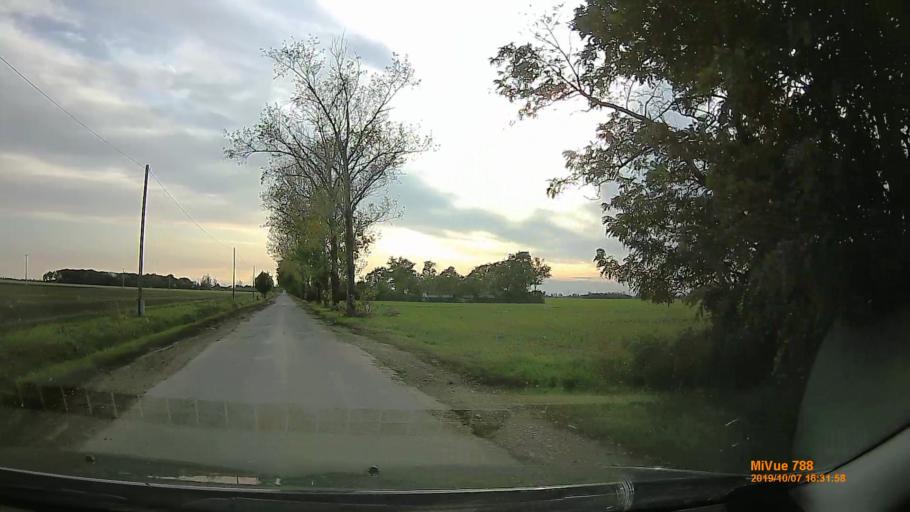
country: HU
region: Bekes
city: Szarvas
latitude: 46.8036
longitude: 20.6378
